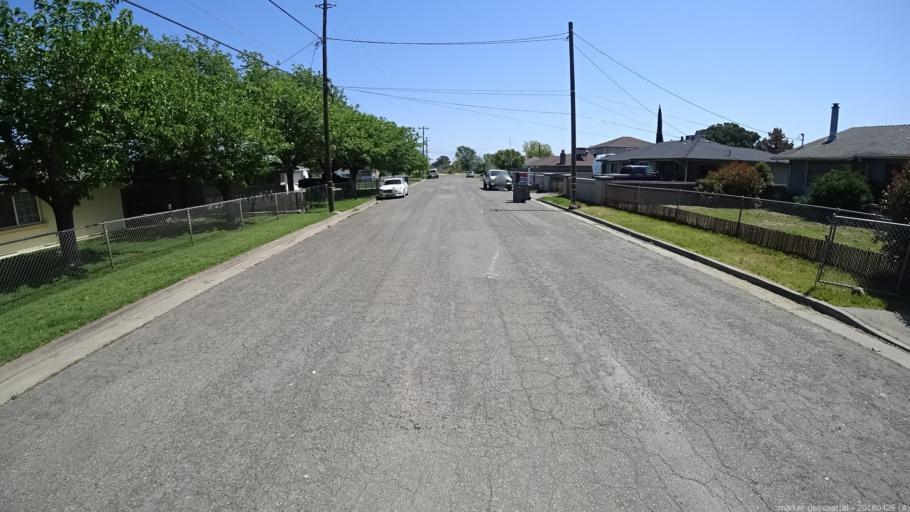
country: US
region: California
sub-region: Yolo County
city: West Sacramento
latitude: 38.5310
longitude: -121.5629
